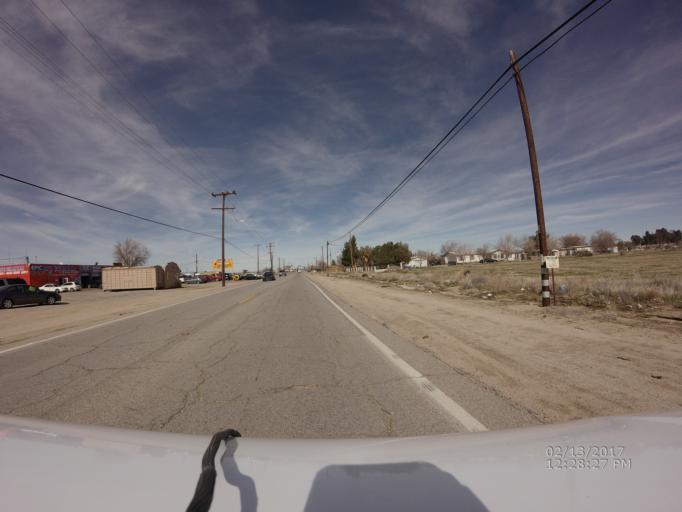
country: US
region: California
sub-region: Los Angeles County
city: Littlerock
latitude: 34.5697
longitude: -117.9697
